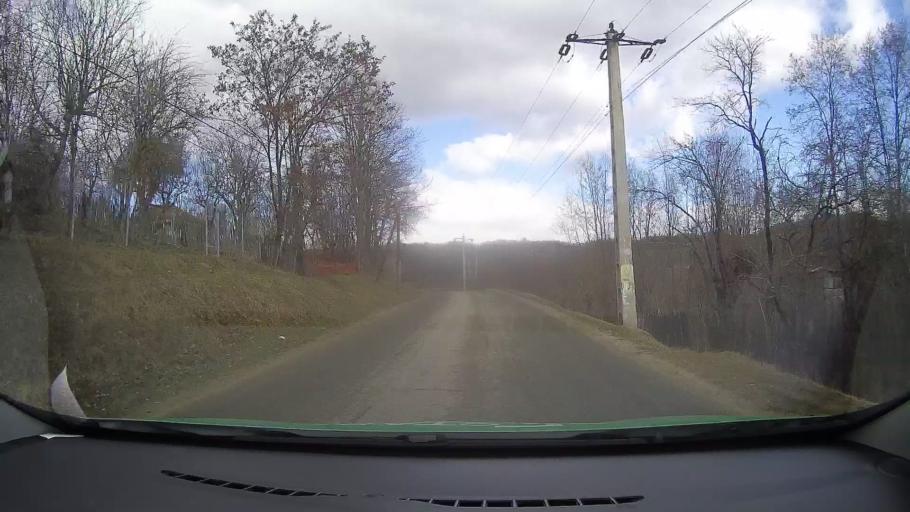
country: RO
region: Dambovita
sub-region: Comuna Buciumeni
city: Buciumeni
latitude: 45.1330
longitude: 25.4677
